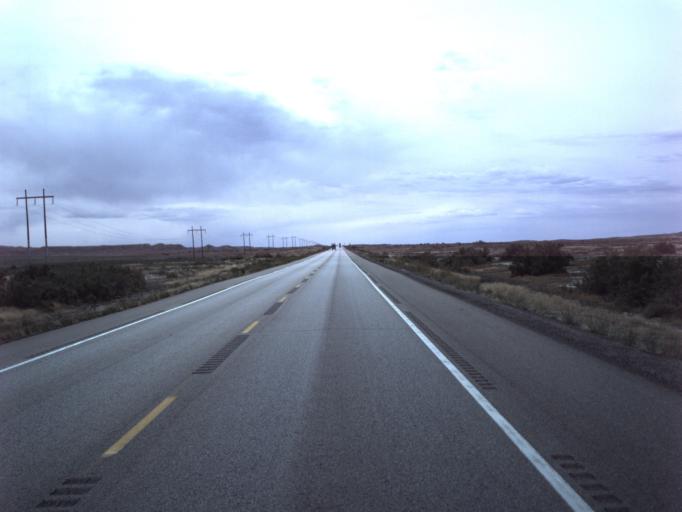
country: US
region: Utah
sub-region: Carbon County
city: East Carbon City
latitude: 39.2352
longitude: -110.3388
